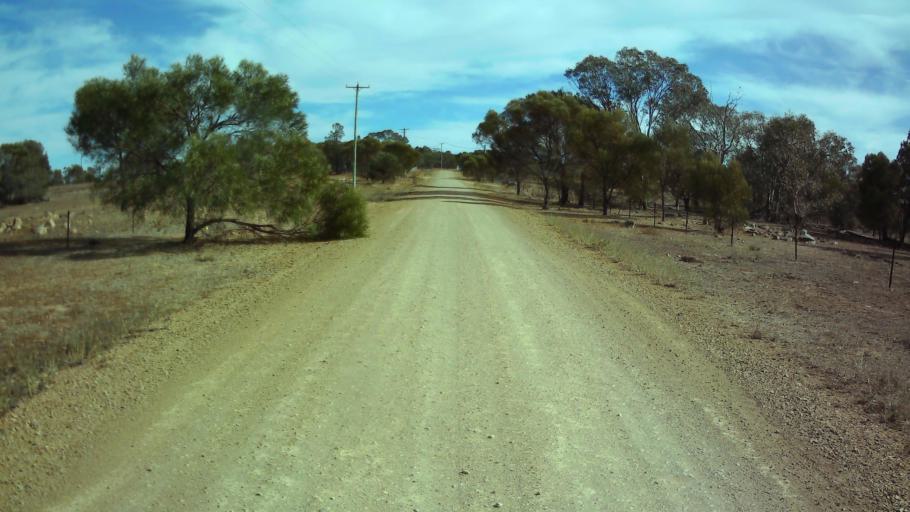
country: AU
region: New South Wales
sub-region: Weddin
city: Grenfell
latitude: -33.8757
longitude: 148.1926
